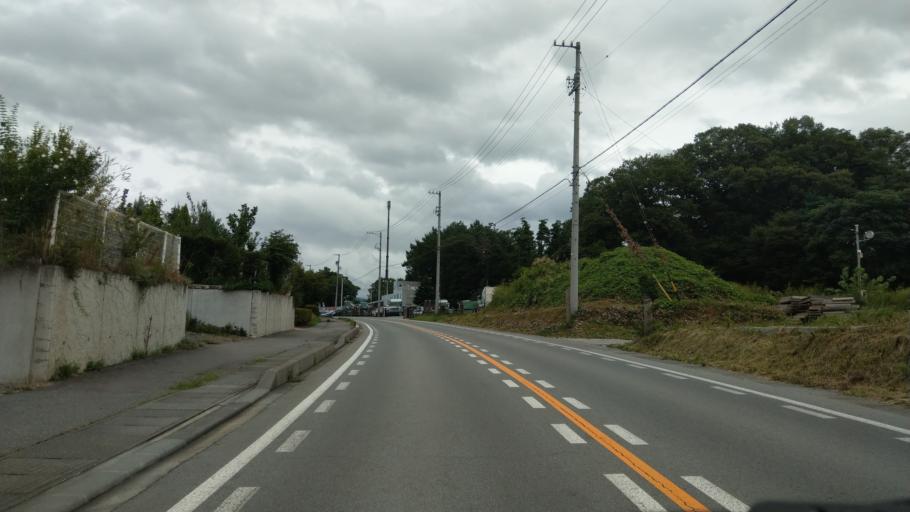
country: JP
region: Nagano
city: Komoro
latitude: 36.2964
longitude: 138.4559
